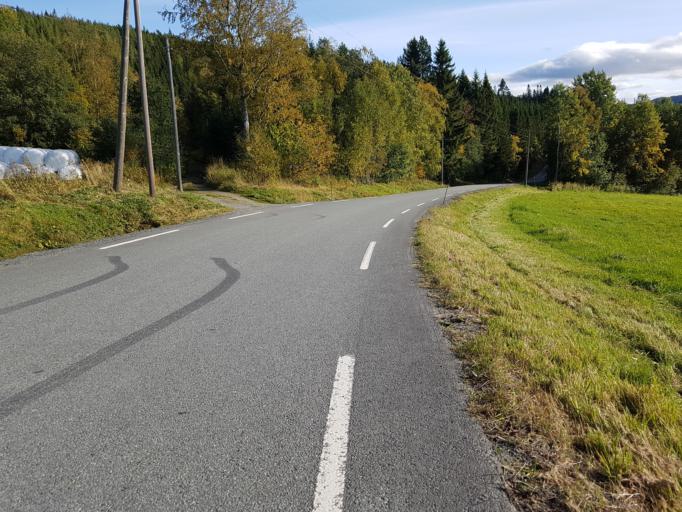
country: NO
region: Sor-Trondelag
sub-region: Malvik
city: Malvik
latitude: 63.3636
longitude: 10.6261
